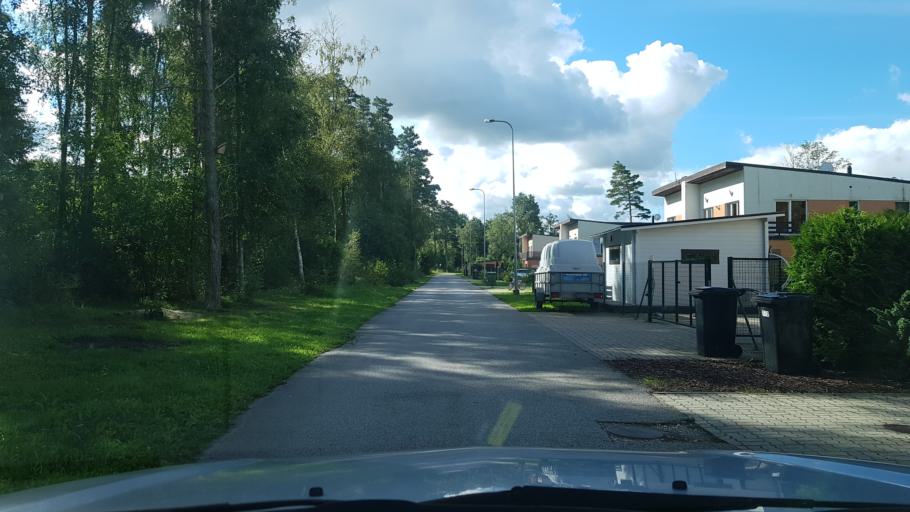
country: EE
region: Harju
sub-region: Kiili vald
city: Kiili
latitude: 59.3667
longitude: 24.8171
